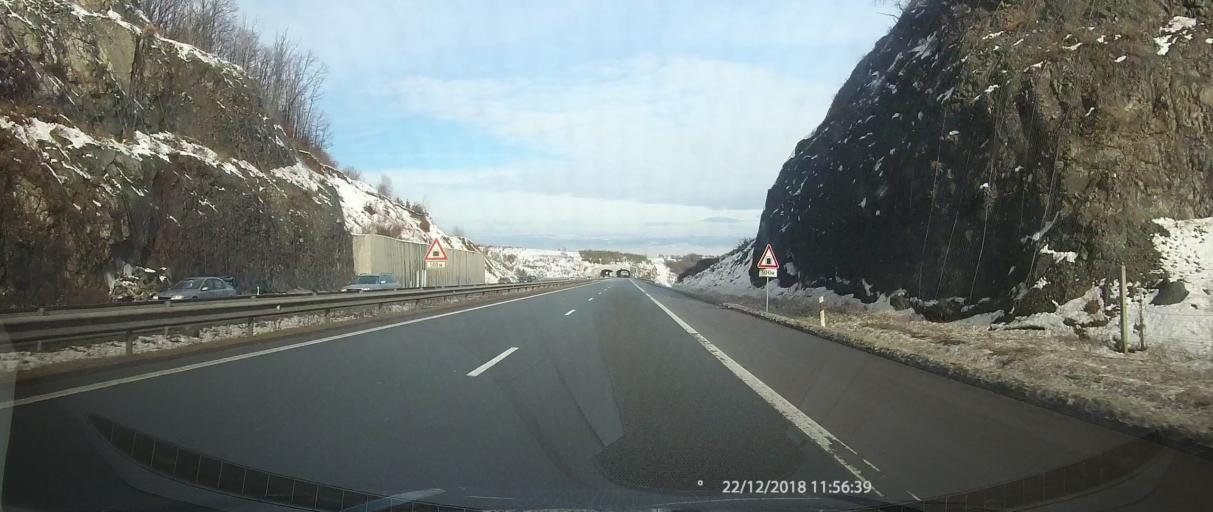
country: BG
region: Sofiya
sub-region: Obshtina Bozhurishte
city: Bozhurishte
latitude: 42.6734
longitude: 23.1513
